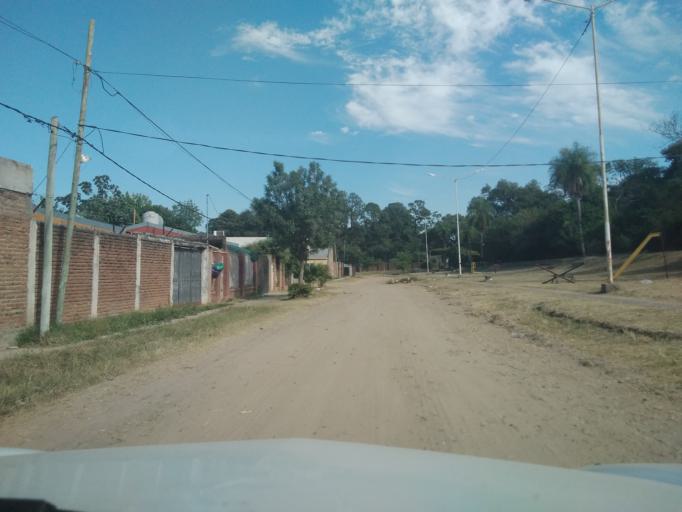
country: AR
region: Corrientes
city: Corrientes
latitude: -27.5091
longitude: -58.7995
